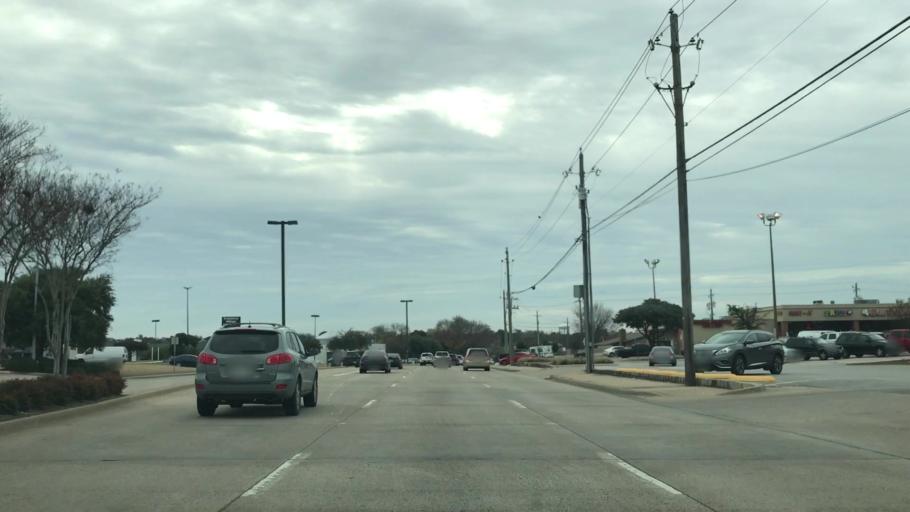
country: US
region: Texas
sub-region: Dallas County
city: Carrollton
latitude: 32.9993
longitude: -96.8868
